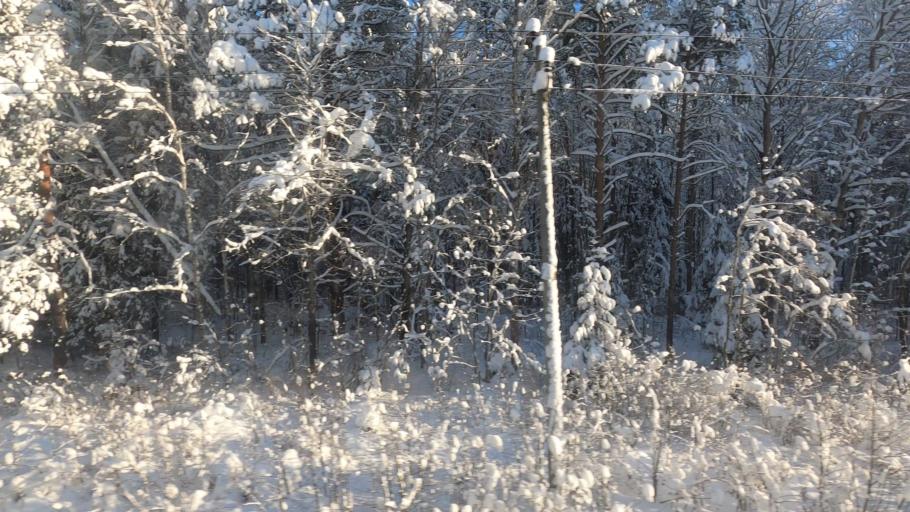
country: RU
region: Moskovskaya
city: Zhukovka
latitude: 56.4889
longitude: 37.5504
